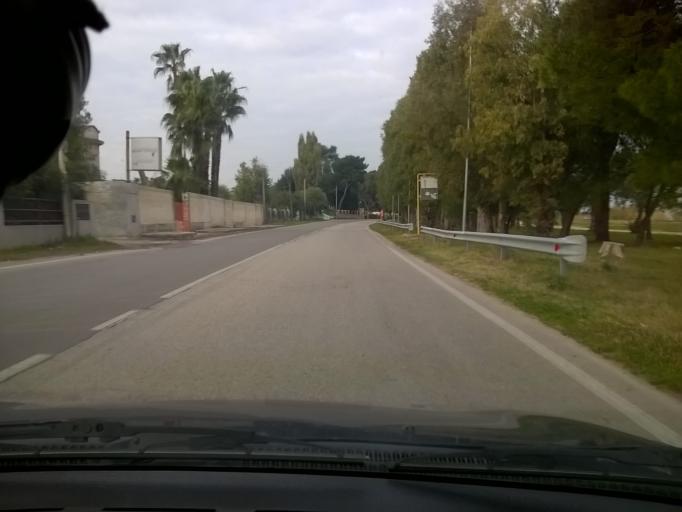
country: IT
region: Apulia
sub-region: Provincia di Taranto
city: Taranto
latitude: 40.4228
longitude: 17.2307
